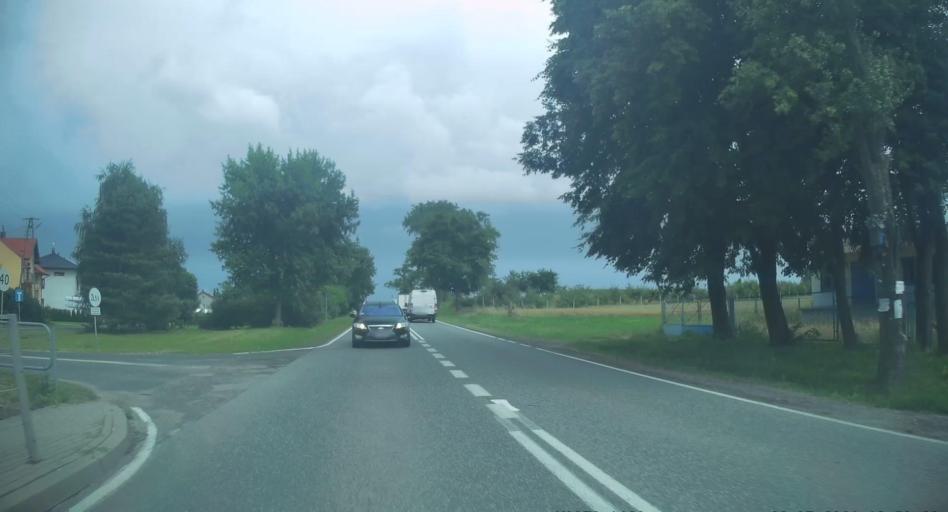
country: PL
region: Lodz Voivodeship
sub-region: Powiat skierniewicki
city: Gluchow
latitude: 51.7716
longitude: 20.1451
